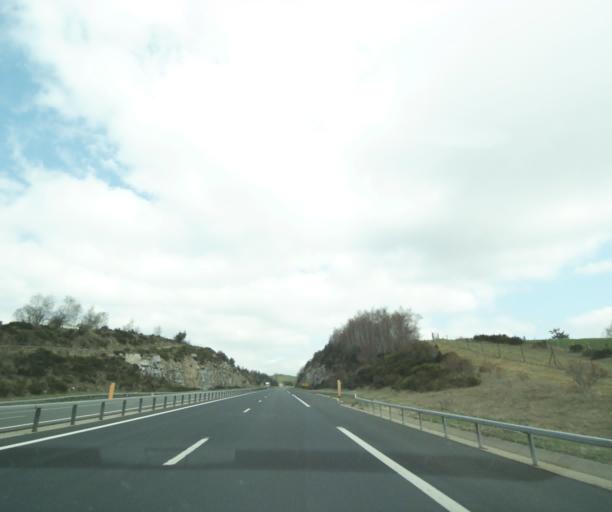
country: FR
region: Languedoc-Roussillon
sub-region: Departement de la Lozere
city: Aumont-Aubrac
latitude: 44.6418
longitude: 3.2425
